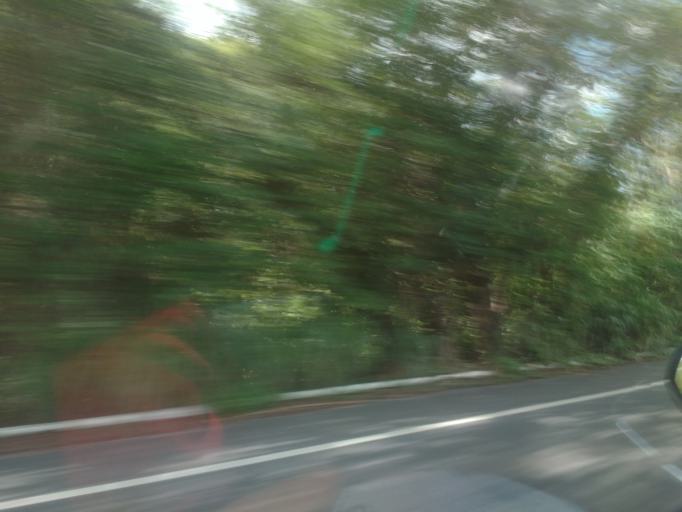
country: BR
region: Alagoas
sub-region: Murici
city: Murici
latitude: -9.2620
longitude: -35.9851
